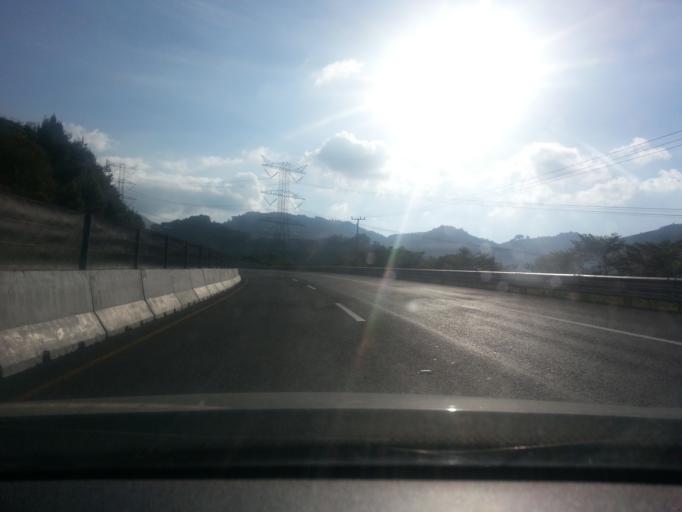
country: MX
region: Puebla
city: Necaxa
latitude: 20.2537
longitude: -98.0230
